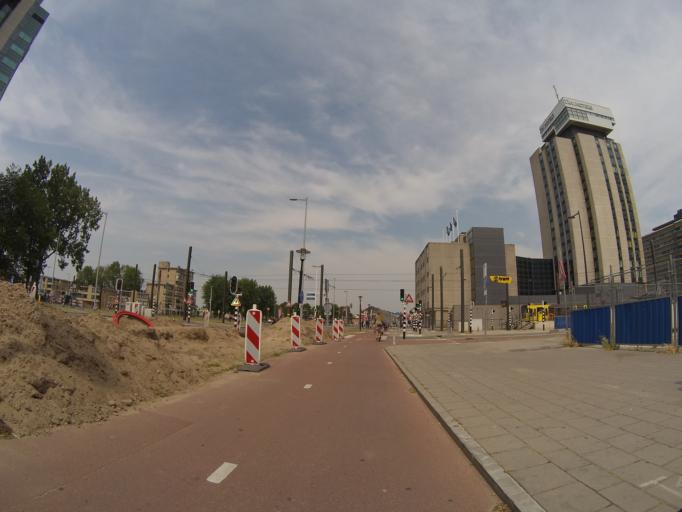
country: NL
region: Utrecht
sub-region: Gemeente Utrecht
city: Utrecht
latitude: 52.0892
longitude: 5.1054
